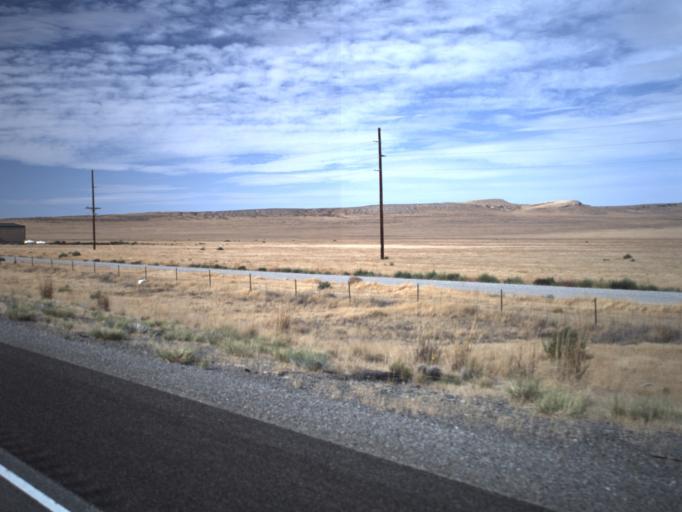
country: US
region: Utah
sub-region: Tooele County
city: Grantsville
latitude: 40.7858
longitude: -112.9617
